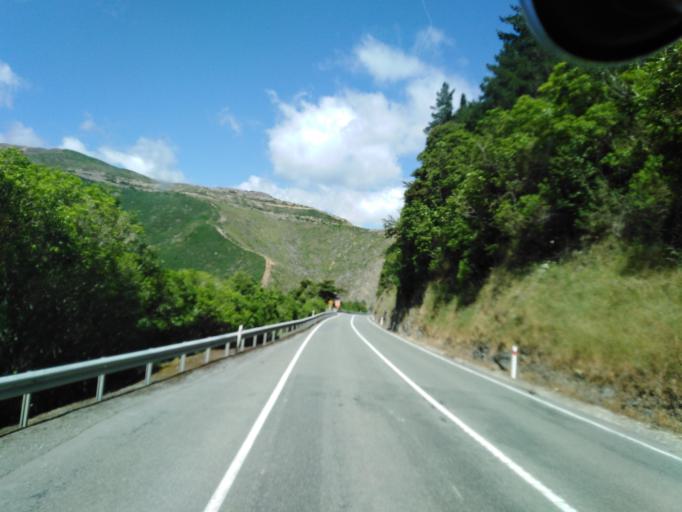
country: NZ
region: Nelson
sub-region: Nelson City
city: Nelson
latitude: -41.2286
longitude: 173.4159
